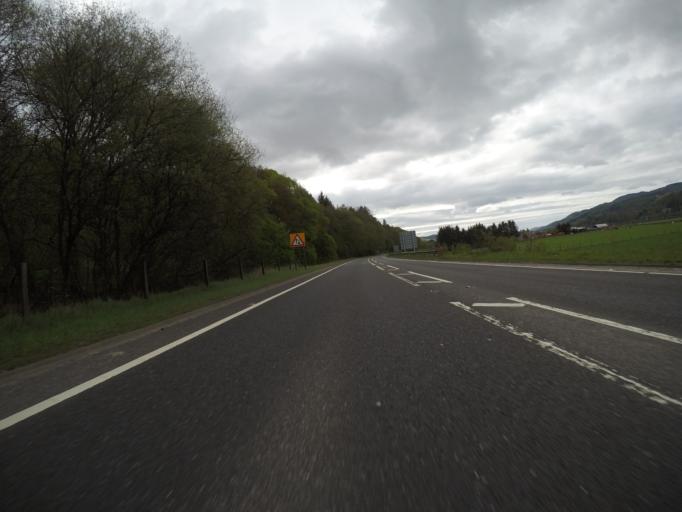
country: GB
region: Scotland
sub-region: Perth and Kinross
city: Pitlochry
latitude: 56.6443
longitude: -3.6553
